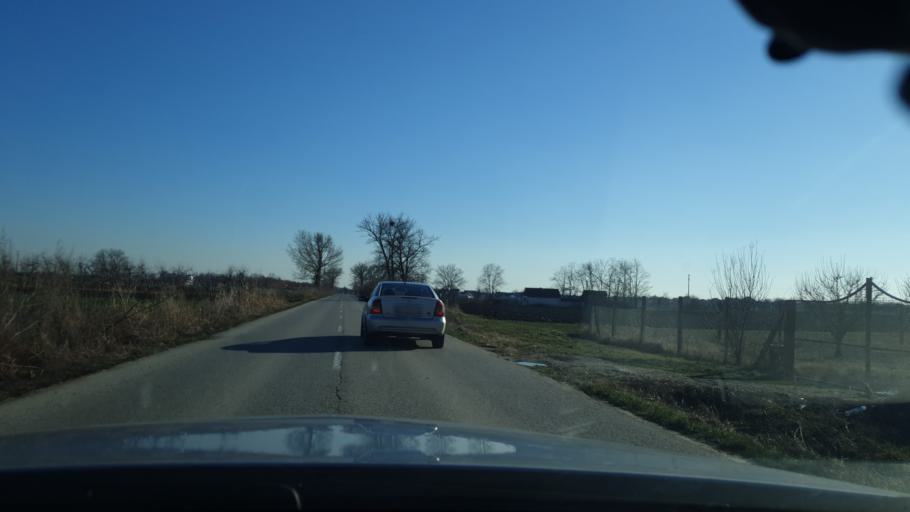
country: RS
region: Autonomna Pokrajina Vojvodina
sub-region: Sremski Okrug
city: Ruma
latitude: 45.0257
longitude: 19.8128
